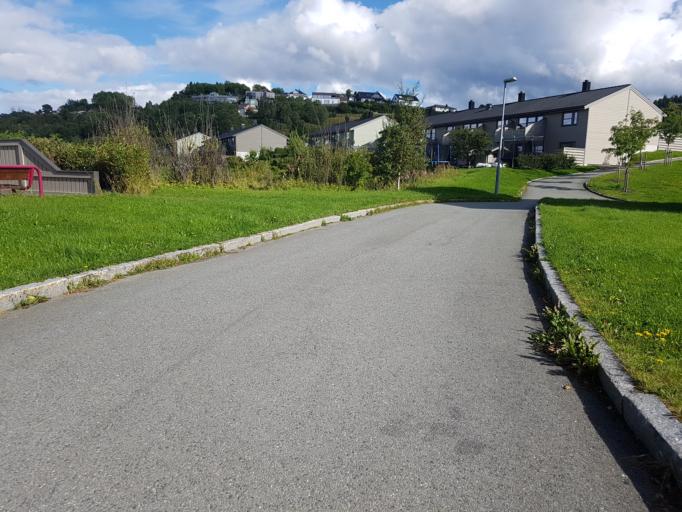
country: NO
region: Sor-Trondelag
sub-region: Trondheim
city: Trondheim
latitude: 63.4034
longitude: 10.4397
